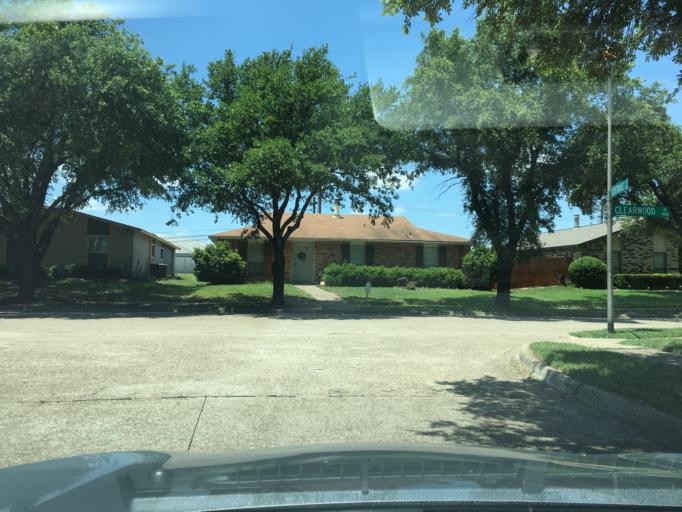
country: US
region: Texas
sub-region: Dallas County
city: Richardson
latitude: 32.9523
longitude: -96.6761
